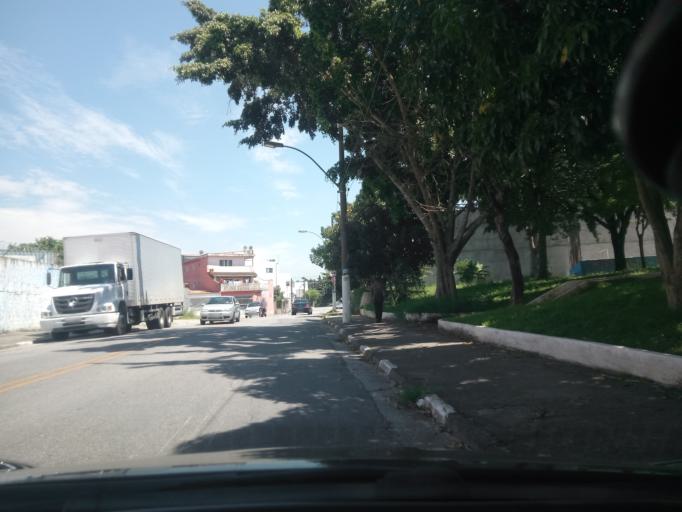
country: BR
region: Sao Paulo
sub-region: Sao Bernardo Do Campo
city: Sao Bernardo do Campo
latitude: -23.7194
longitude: -46.5810
